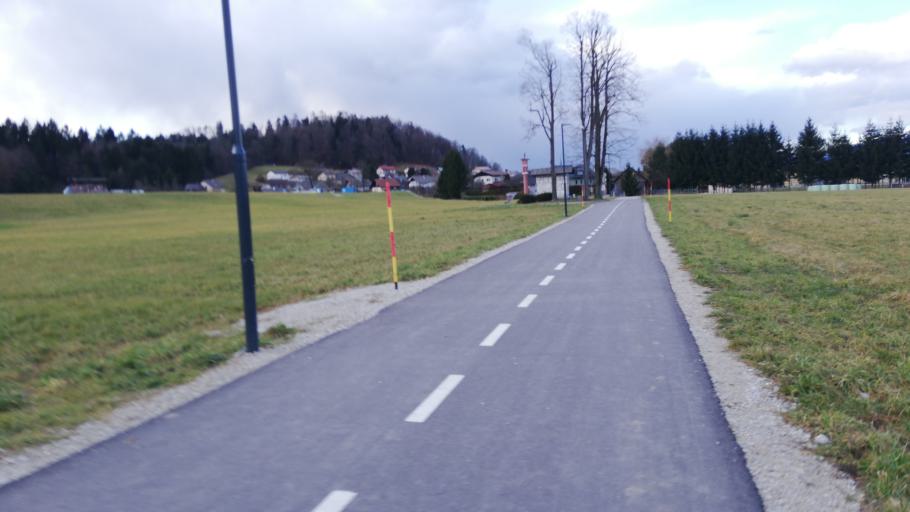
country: SI
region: Medvode
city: Medvode
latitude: 46.1280
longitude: 14.4158
